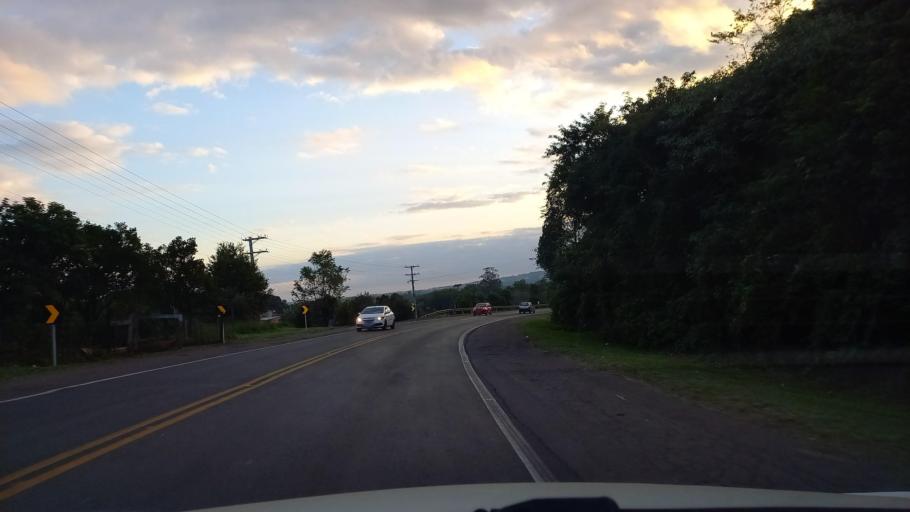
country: BR
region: Rio Grande do Sul
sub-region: Santa Cruz Do Sul
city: Santa Cruz do Sul
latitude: -29.6846
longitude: -52.4381
